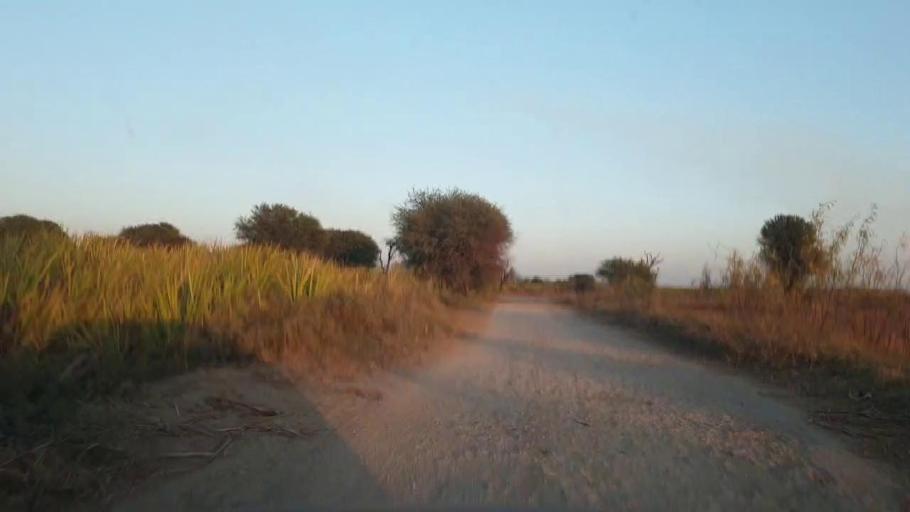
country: PK
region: Sindh
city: Chambar
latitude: 25.3642
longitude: 68.7408
